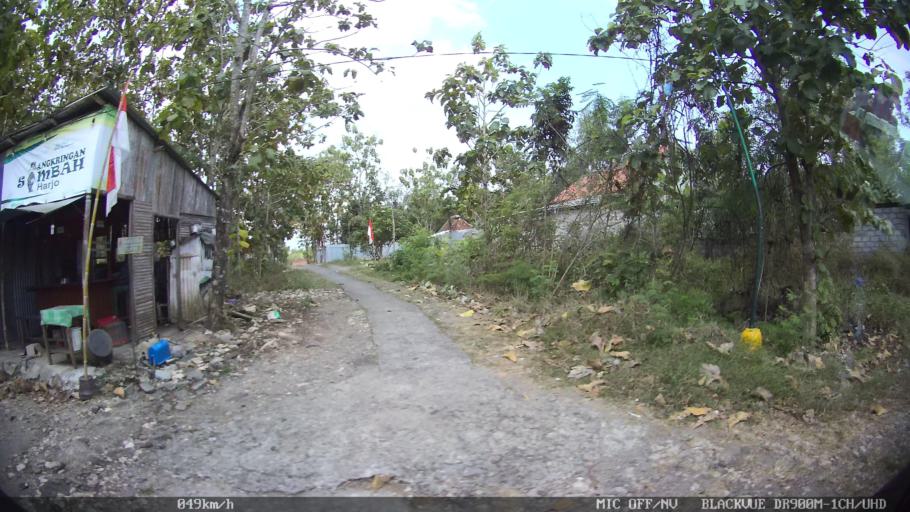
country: ID
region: Daerah Istimewa Yogyakarta
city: Kasihan
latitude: -7.8556
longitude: 110.3104
